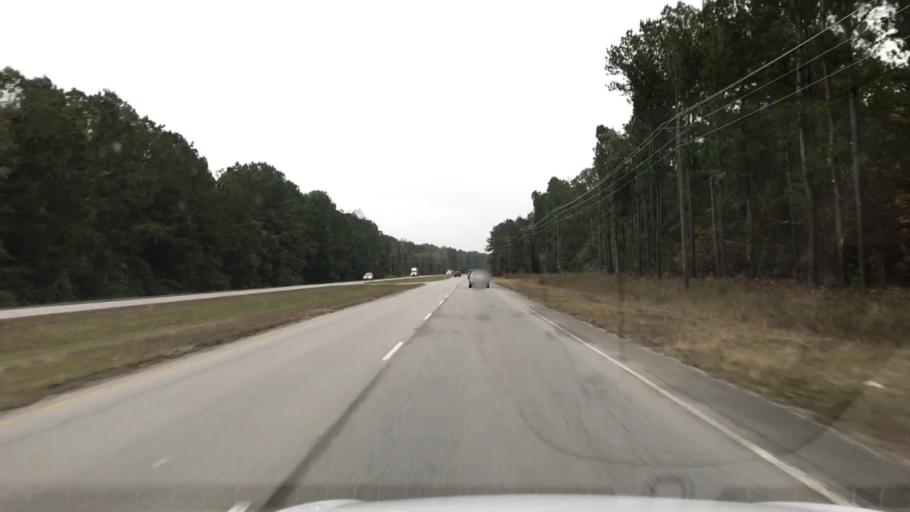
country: US
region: South Carolina
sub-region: Charleston County
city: Awendaw
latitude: 32.9518
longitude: -79.6957
